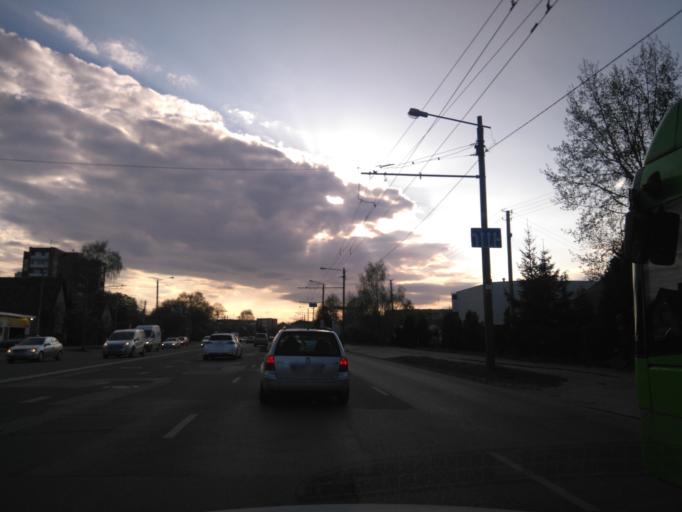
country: LT
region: Kauno apskritis
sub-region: Kaunas
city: Eiguliai
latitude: 54.9113
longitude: 23.9446
